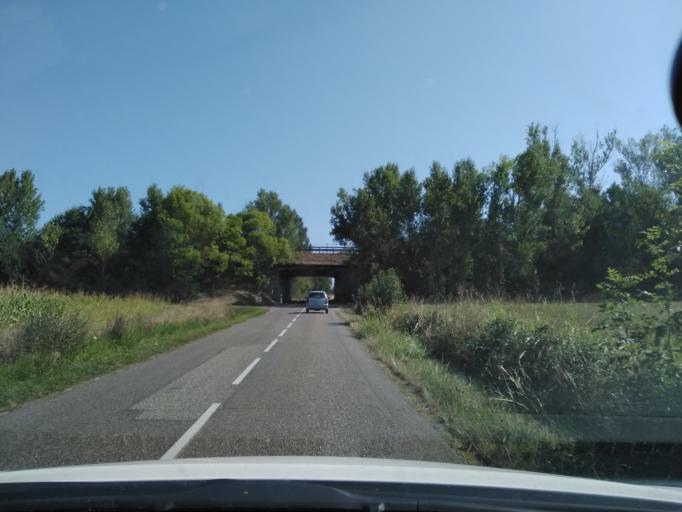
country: FR
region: Midi-Pyrenees
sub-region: Departement du Tarn-et-Garonne
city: Montech
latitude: 43.9812
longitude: 1.2512
